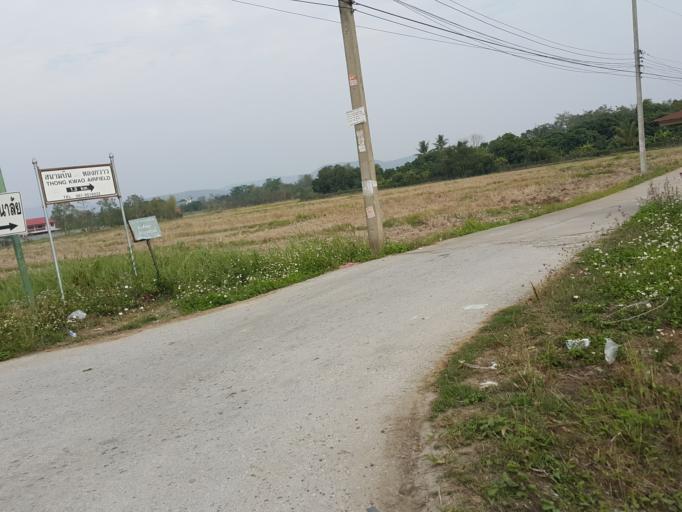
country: TH
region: Chiang Mai
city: San Kamphaeng
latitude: 18.8272
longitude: 99.1269
